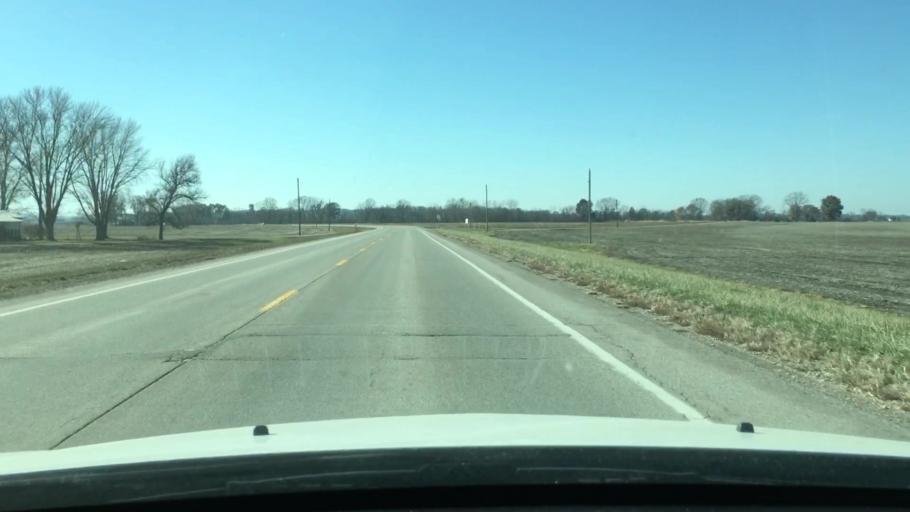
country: US
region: Missouri
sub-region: Pike County
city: Louisiana
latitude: 39.5002
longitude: -90.9972
